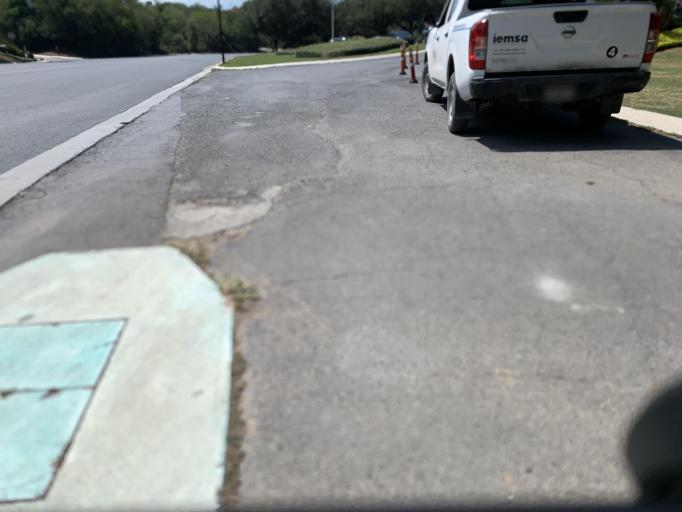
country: MX
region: Nuevo Leon
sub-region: Juarez
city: Bosques de San Pedro
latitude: 25.5167
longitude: -100.1914
